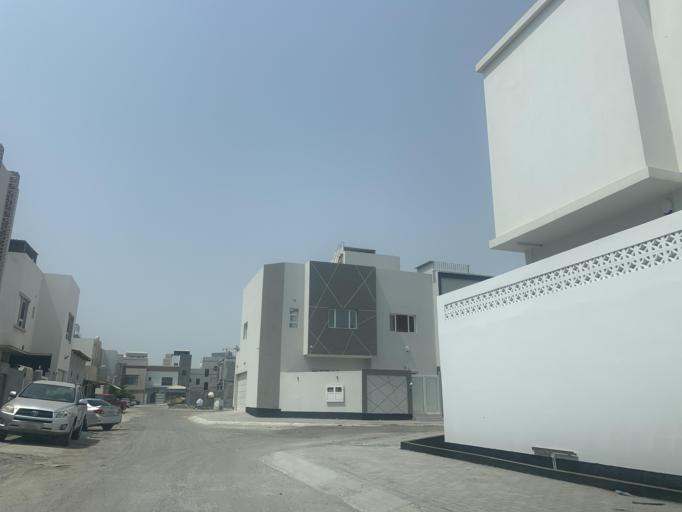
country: BH
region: Central Governorate
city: Madinat Hamad
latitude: 26.1304
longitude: 50.4675
